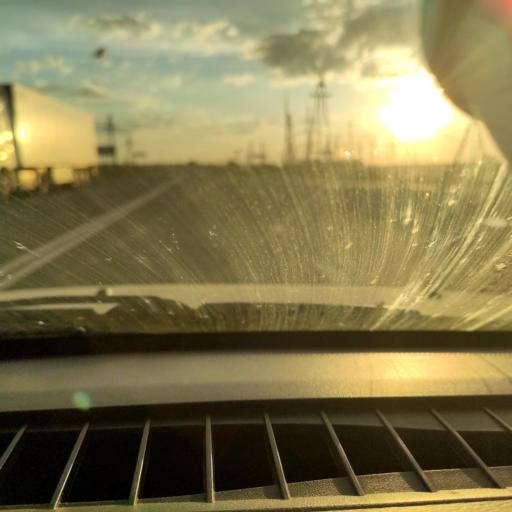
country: RU
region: Kirov
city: Kotel'nich
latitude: 58.3197
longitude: 48.3930
